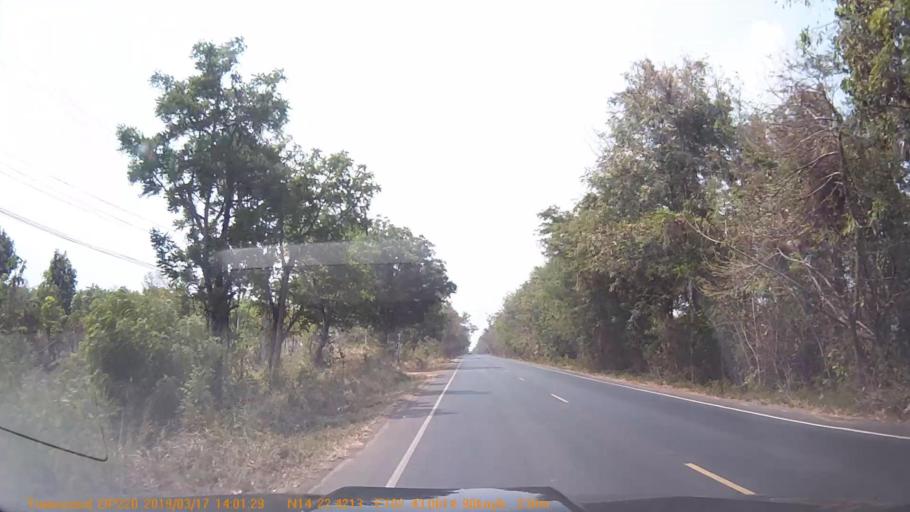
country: TH
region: Buriram
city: Pa Kham
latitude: 14.3739
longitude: 102.7175
